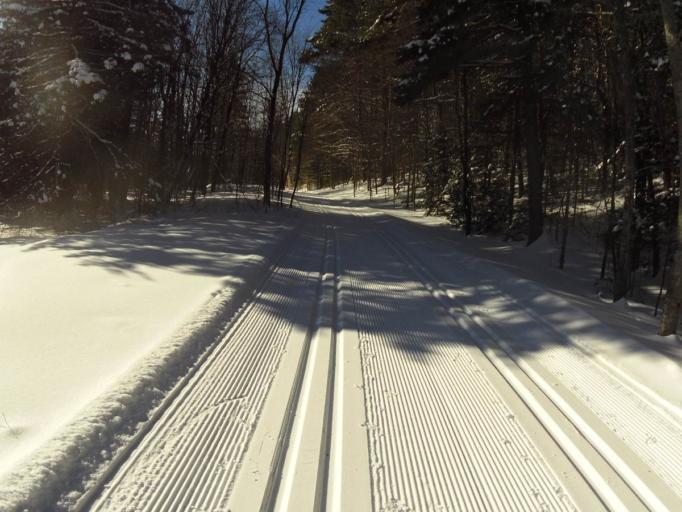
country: CA
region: Quebec
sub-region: Outaouais
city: Wakefield
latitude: 45.6246
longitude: -76.0077
